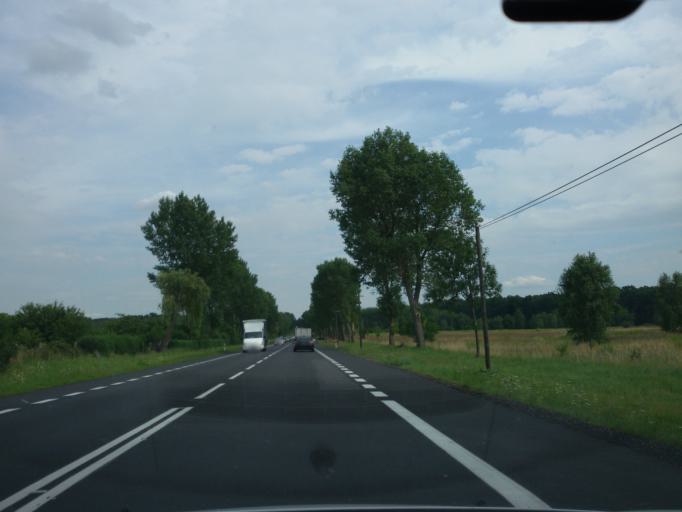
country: PL
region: Lubusz
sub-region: Powiat nowosolski
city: Nowe Miasteczko
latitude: 51.6870
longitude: 15.7438
